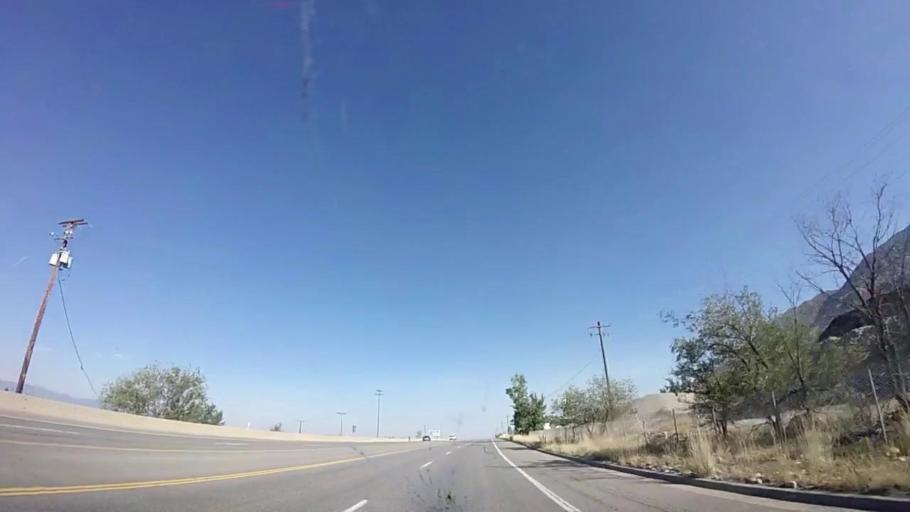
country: US
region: Utah
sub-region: Salt Lake County
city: Cottonwood Heights
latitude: 40.6253
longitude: -111.7962
